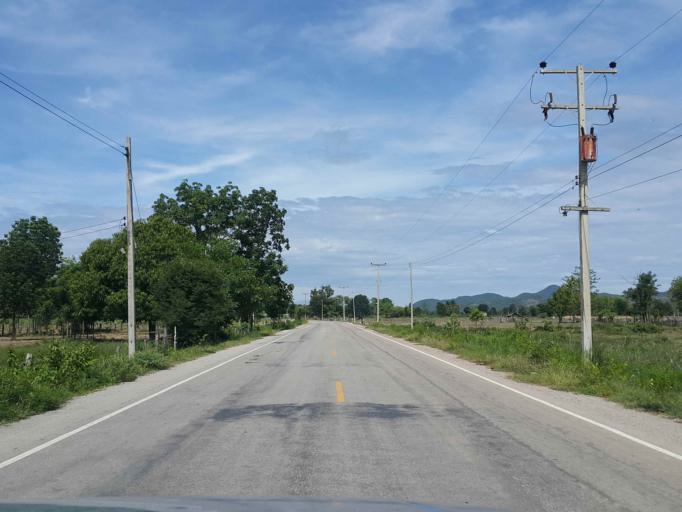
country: TH
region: Sukhothai
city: Ban Dan Lan Hoi
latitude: 17.1153
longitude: 99.5225
